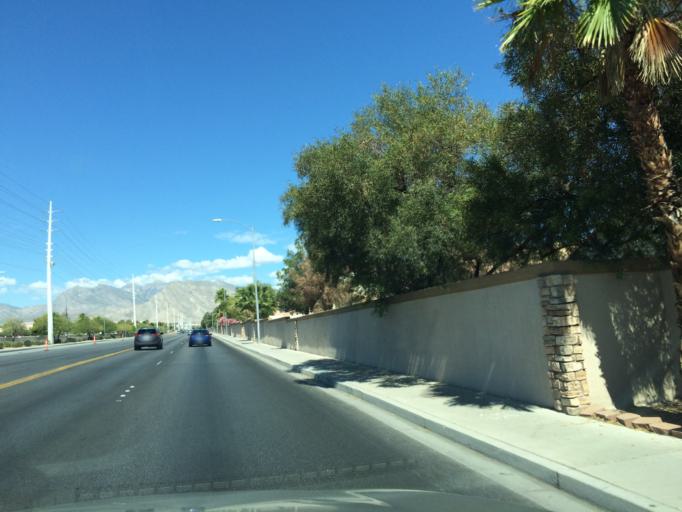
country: US
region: Nevada
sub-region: Clark County
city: Spring Valley
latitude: 36.2185
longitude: -115.2659
